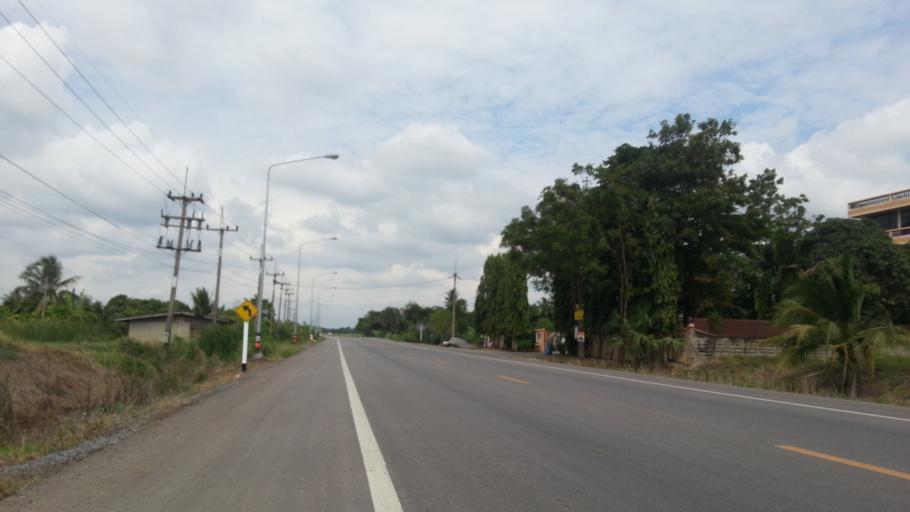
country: TH
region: Pathum Thani
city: Ban Rangsit
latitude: 14.0409
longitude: 100.8442
